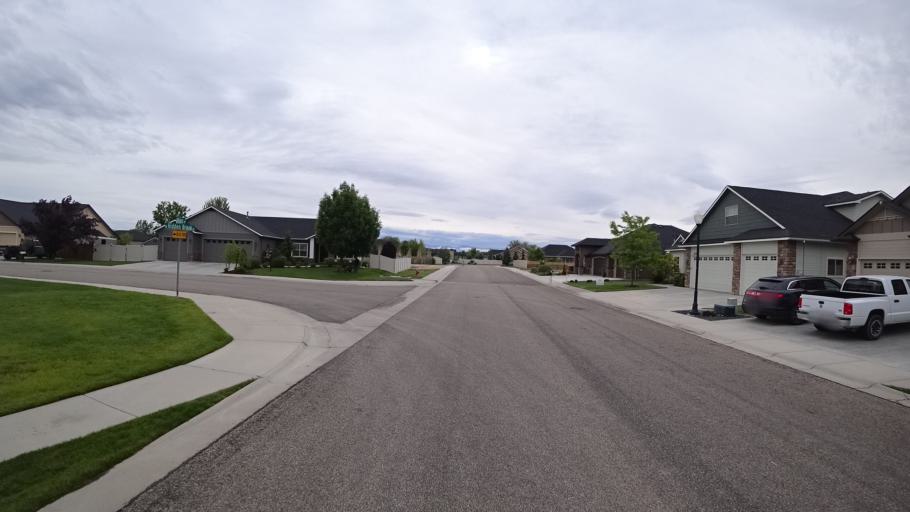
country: US
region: Idaho
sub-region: Ada County
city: Star
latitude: 43.7004
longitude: -116.4883
